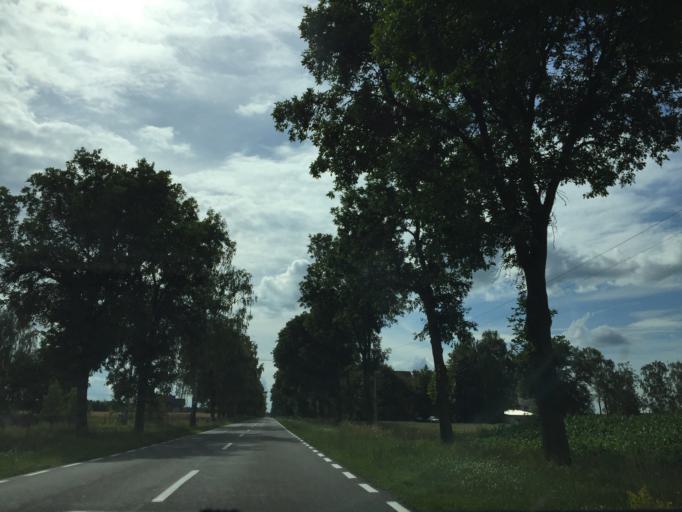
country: PL
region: Lublin Voivodeship
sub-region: Powiat lukowski
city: Trzebieszow
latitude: 51.9872
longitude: 22.6038
